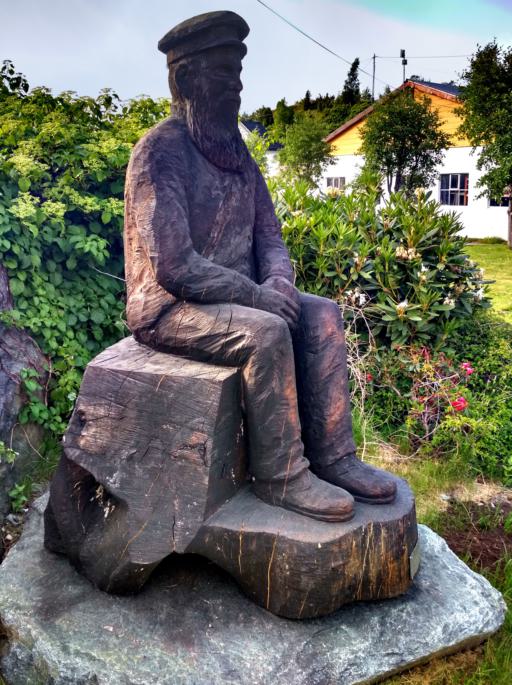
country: NO
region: Hordaland
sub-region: Osteroy
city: Lonevag
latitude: 60.5903
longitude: 5.5246
